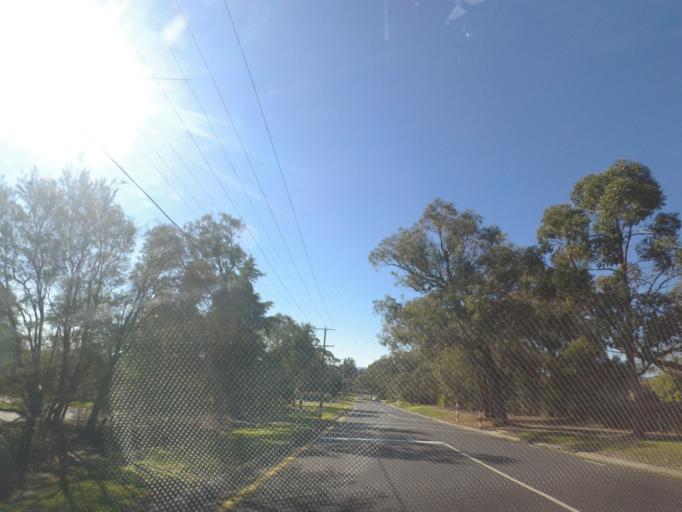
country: AU
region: Victoria
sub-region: Maroondah
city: Croydon Hills
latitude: -37.7762
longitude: 145.2752
